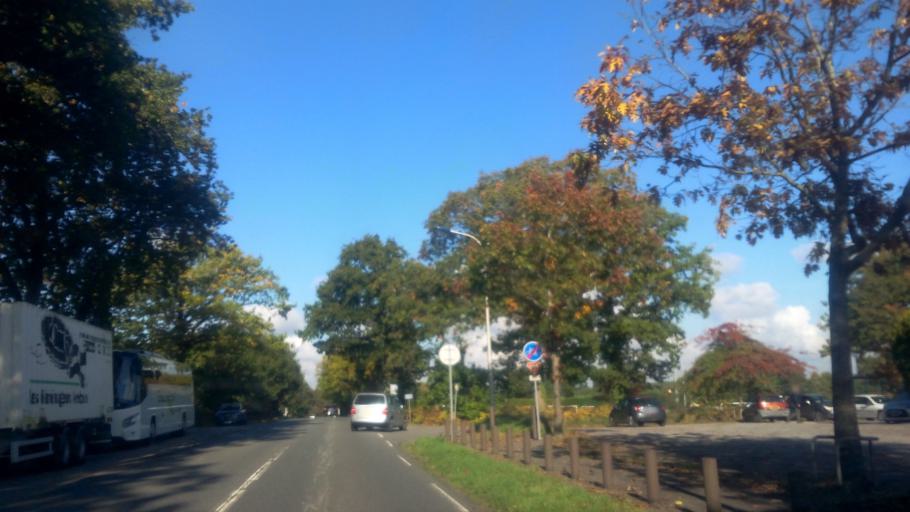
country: FR
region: Brittany
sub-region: Departement d'Ille-et-Vilaine
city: Redon
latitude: 47.6693
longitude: -2.0775
